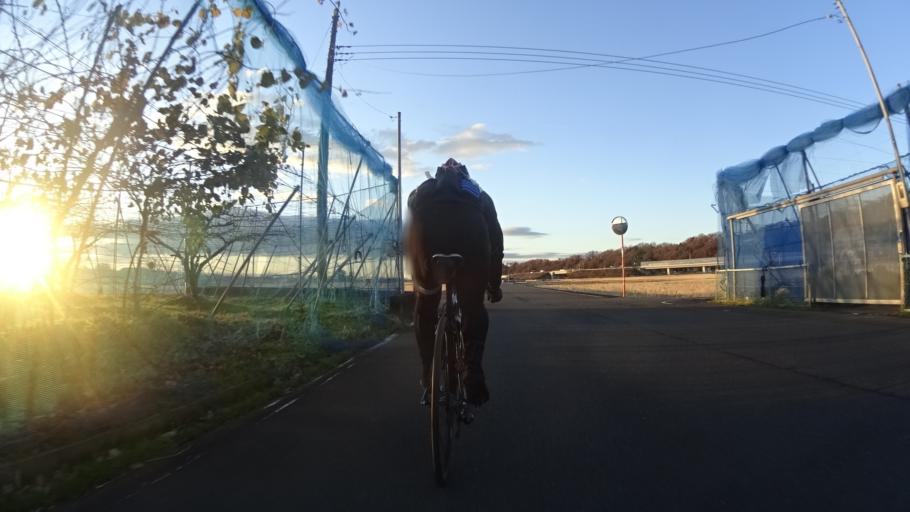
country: JP
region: Kanagawa
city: Zama
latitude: 35.5113
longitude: 139.3677
